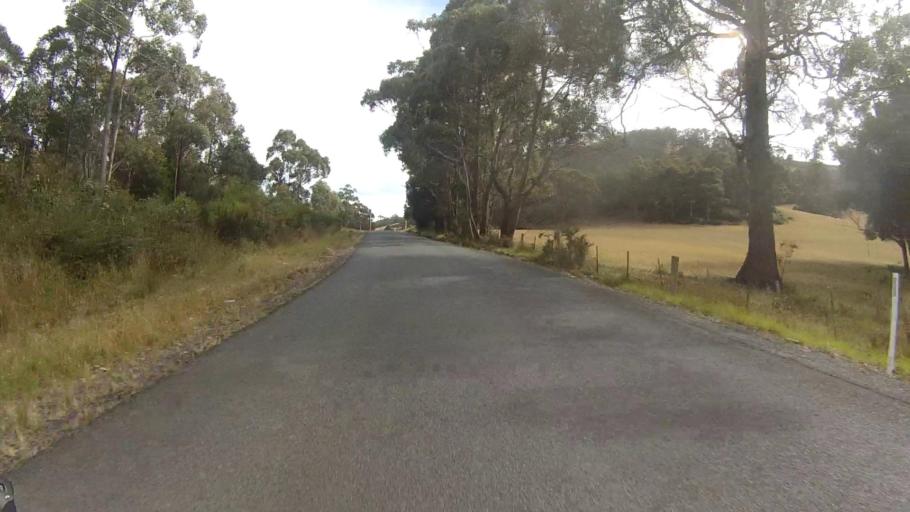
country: AU
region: Tasmania
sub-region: Sorell
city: Sorell
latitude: -42.8103
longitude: 147.7944
